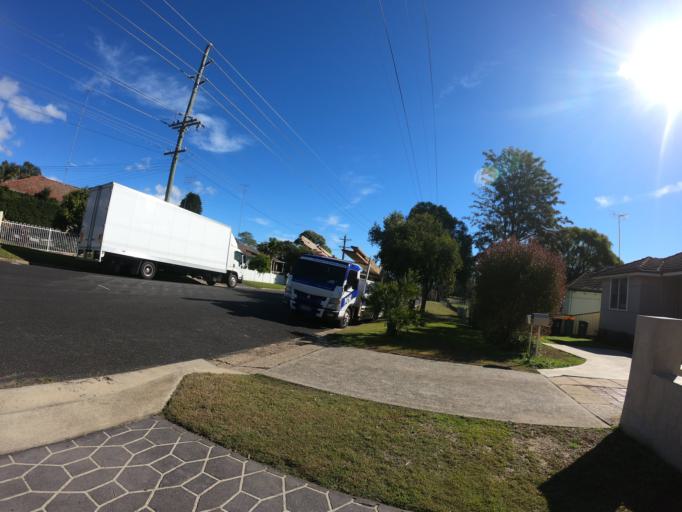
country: AU
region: New South Wales
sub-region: Hawkesbury
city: South Windsor
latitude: -33.6231
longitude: 150.8001
